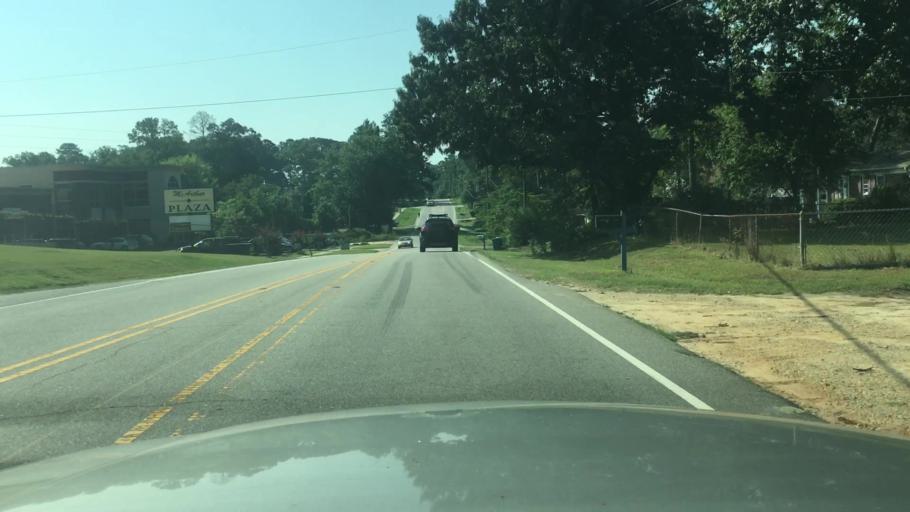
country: US
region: North Carolina
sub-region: Cumberland County
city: Fayetteville
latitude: 35.1224
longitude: -78.8860
